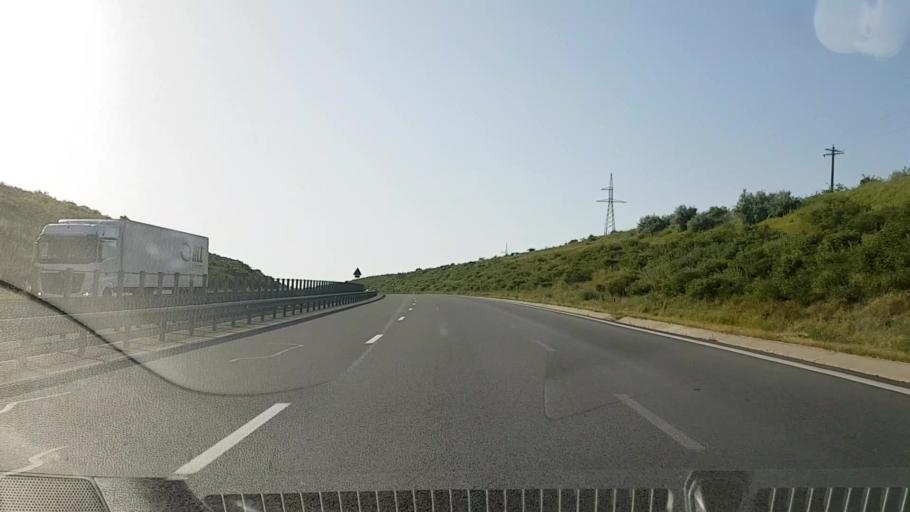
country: RO
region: Cluj
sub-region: Comuna Sandulesti
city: Sandulesti
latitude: 46.5993
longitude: 23.7076
